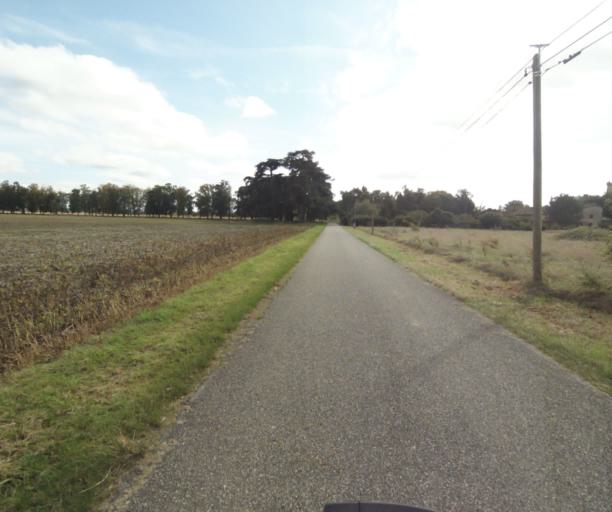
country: FR
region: Midi-Pyrenees
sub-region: Departement du Tarn-et-Garonne
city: Finhan
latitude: 43.9293
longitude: 1.2170
